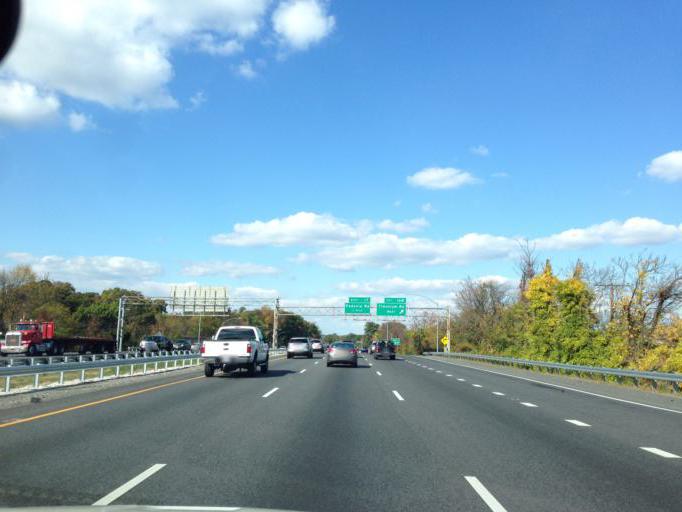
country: US
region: Maryland
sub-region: Baltimore County
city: Timonium
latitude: 39.4382
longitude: -76.6337
